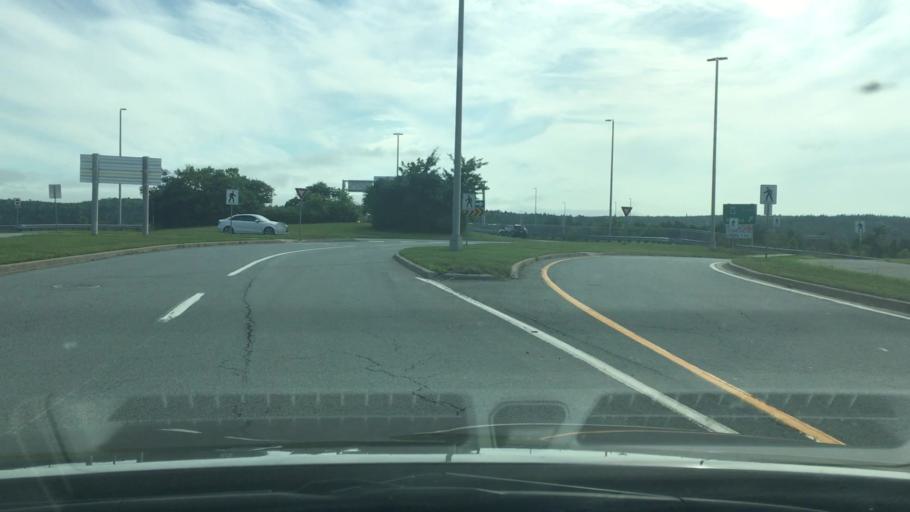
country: CA
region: Nova Scotia
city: Dartmouth
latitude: 44.6997
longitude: -63.6893
